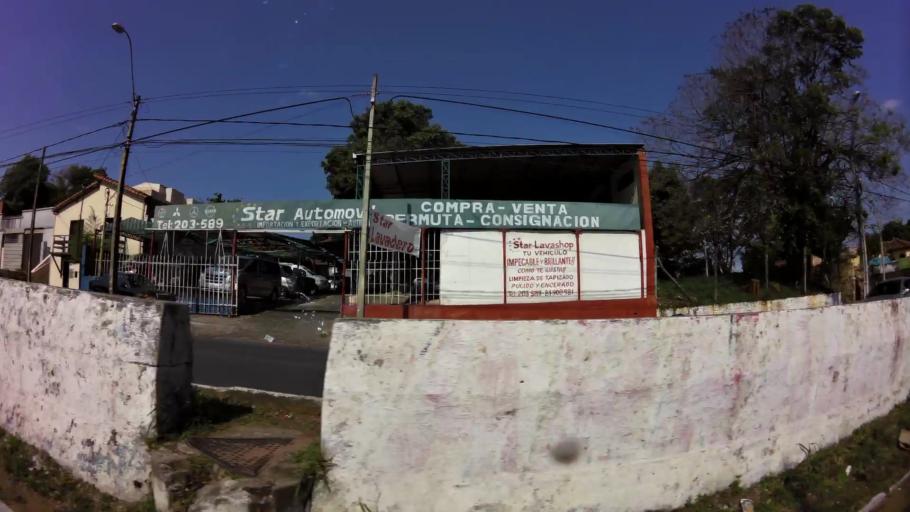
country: PY
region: Asuncion
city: Asuncion
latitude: -25.3041
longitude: -57.6321
